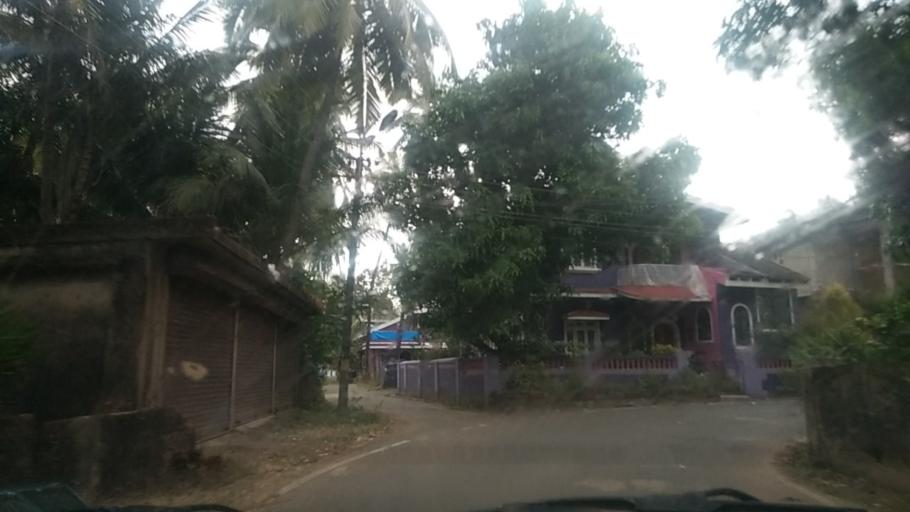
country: IN
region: Goa
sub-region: South Goa
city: Cuncolim
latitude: 15.1926
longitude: 73.9845
